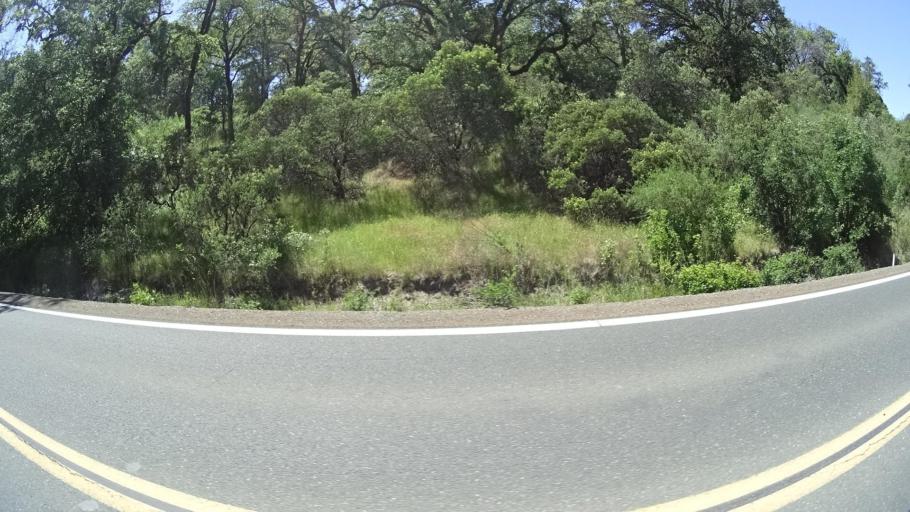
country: US
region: California
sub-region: Lake County
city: North Lakeport
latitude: 39.1191
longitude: -122.8895
